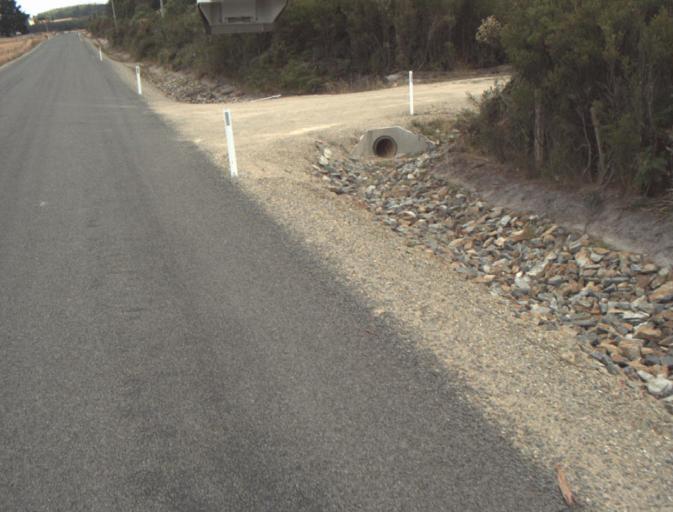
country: AU
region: Tasmania
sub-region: Launceston
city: Mayfield
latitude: -41.2121
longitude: 147.1893
